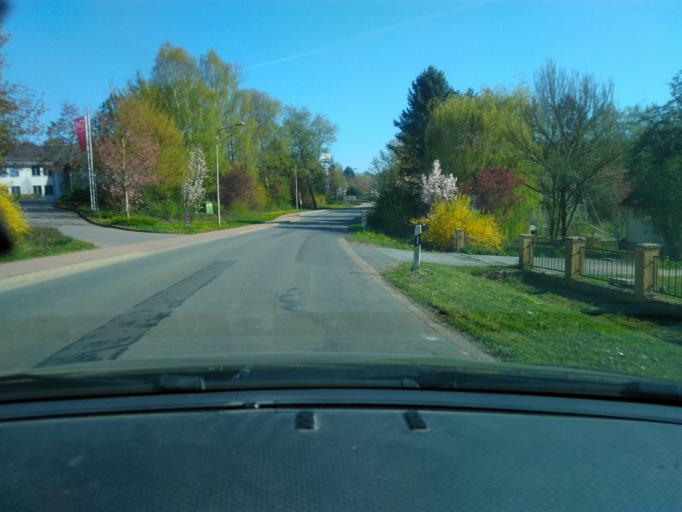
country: DE
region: Lower Saxony
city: Osterode am Harz
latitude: 51.7189
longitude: 10.2713
